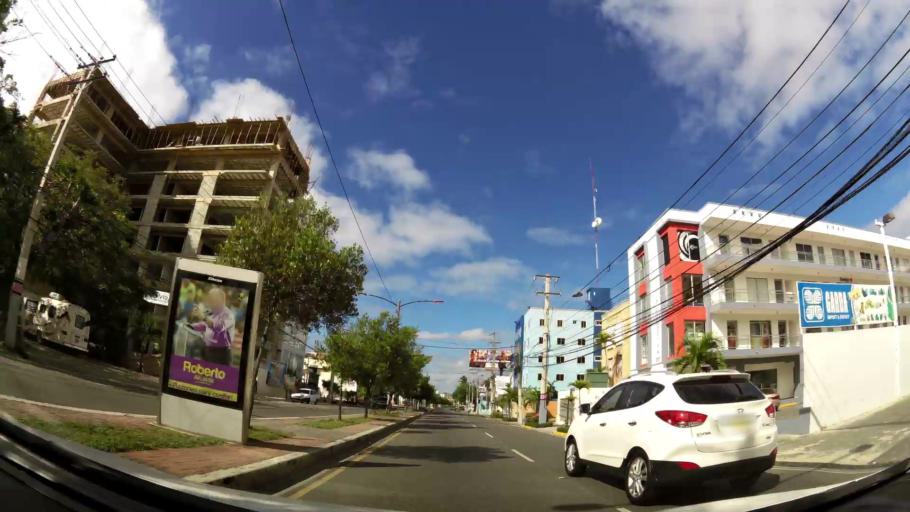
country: DO
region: Nacional
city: Bella Vista
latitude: 18.4582
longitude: -69.9386
